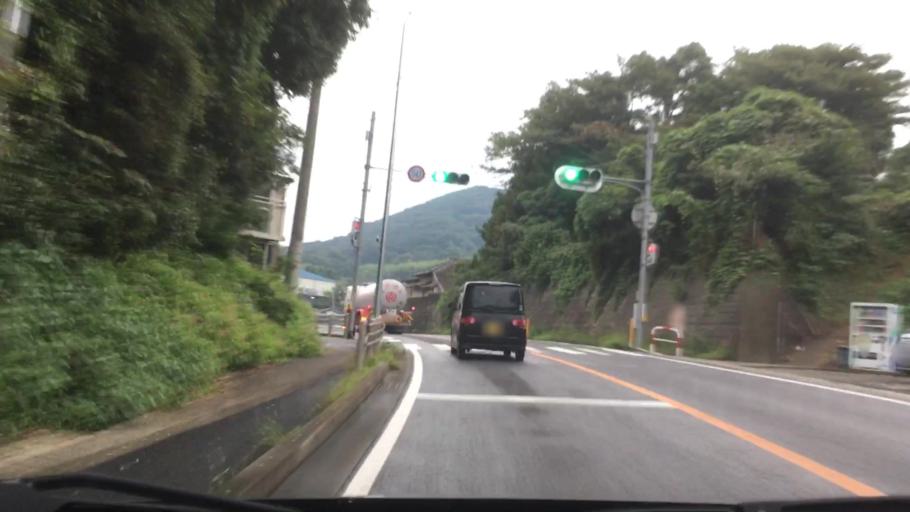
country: JP
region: Nagasaki
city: Sasebo
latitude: 33.1036
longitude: 129.7741
